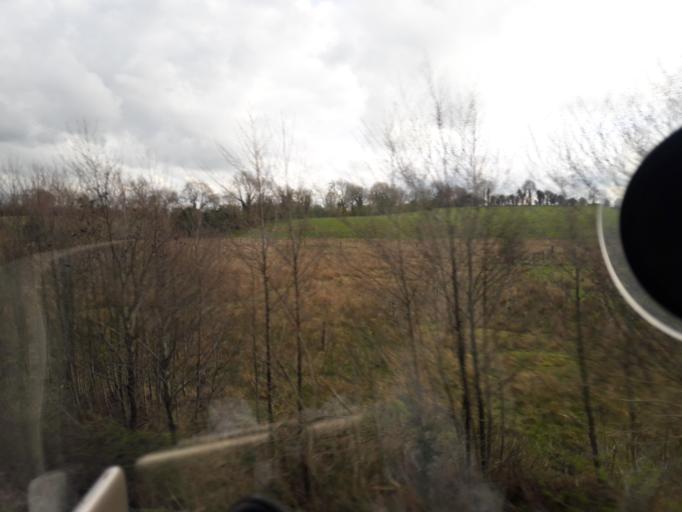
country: IE
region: Leinster
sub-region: An Iarmhi
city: An Muileann gCearr
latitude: 53.5047
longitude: -7.2816
